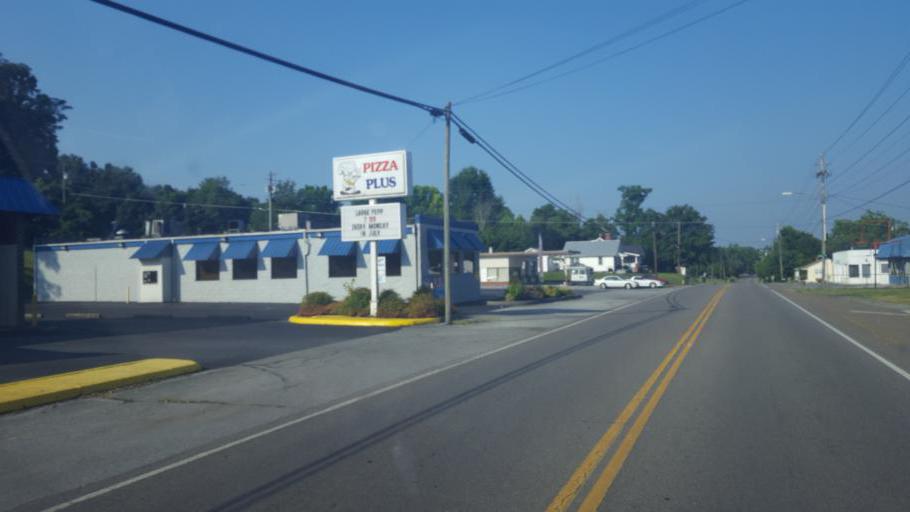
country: US
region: Tennessee
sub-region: Sullivan County
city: Bluff City
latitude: 36.4723
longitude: -82.2686
